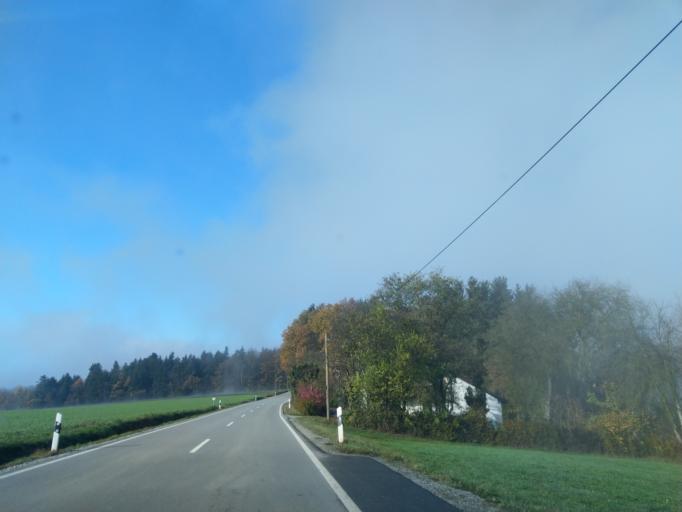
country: DE
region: Bavaria
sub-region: Lower Bavaria
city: Schollnach
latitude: 48.7342
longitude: 13.1655
